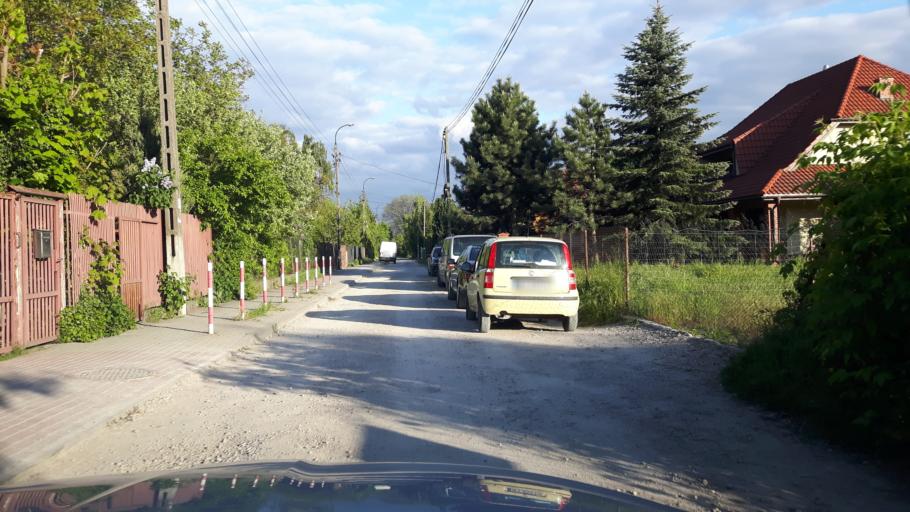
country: PL
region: Masovian Voivodeship
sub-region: Warszawa
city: Targowek
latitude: 52.2759
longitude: 21.0695
